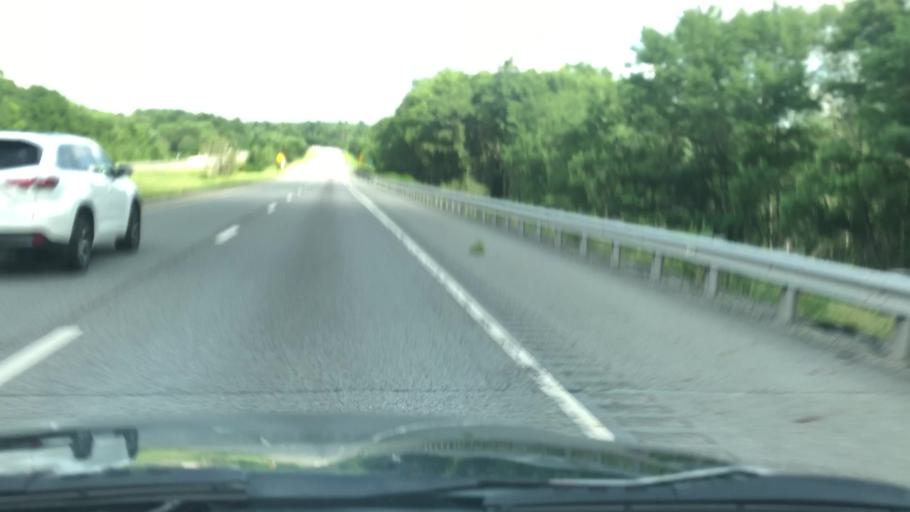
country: US
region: Pennsylvania
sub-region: Pike County
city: Gold Key Lake
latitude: 41.3447
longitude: -74.9254
